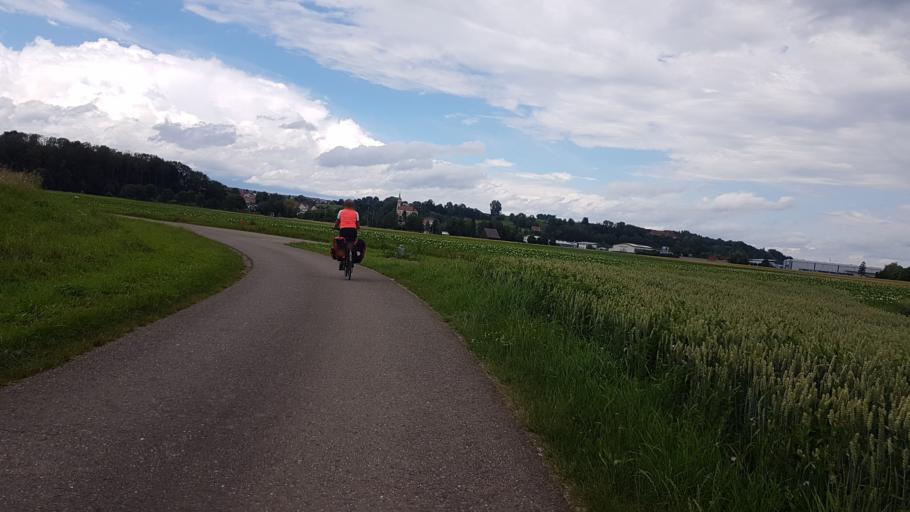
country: DE
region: Baden-Wuerttemberg
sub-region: Tuebingen Region
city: Herbertingen
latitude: 48.0999
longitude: 9.4232
